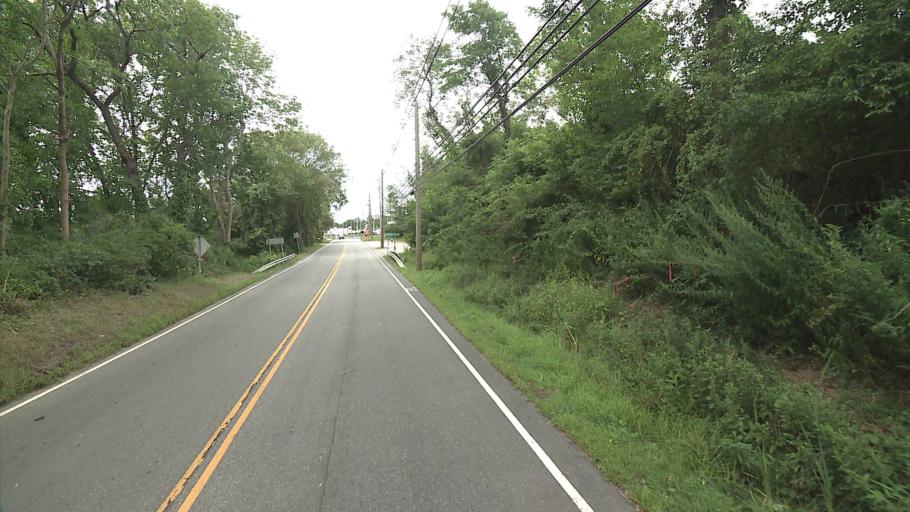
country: US
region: Connecticut
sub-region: New London County
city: Colchester
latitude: 41.5648
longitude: -72.3217
